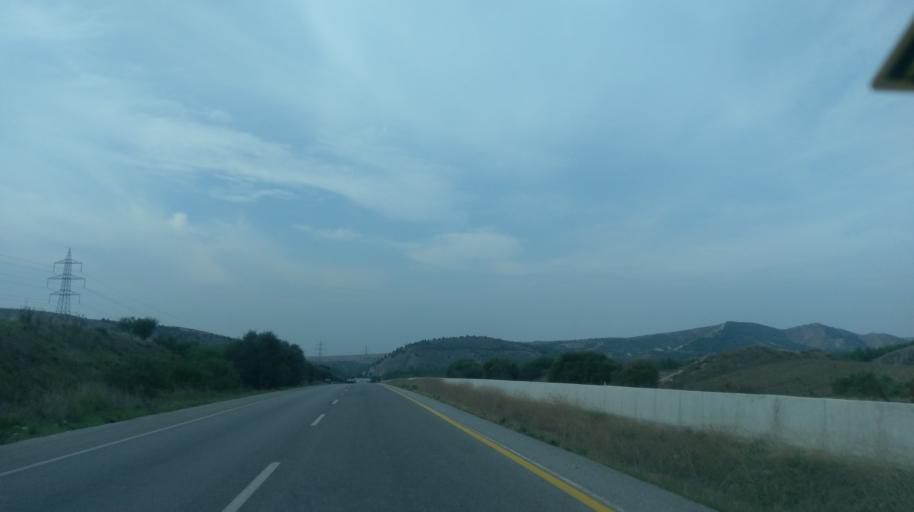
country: CY
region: Lefkosia
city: Mammari
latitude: 35.2145
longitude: 33.1333
